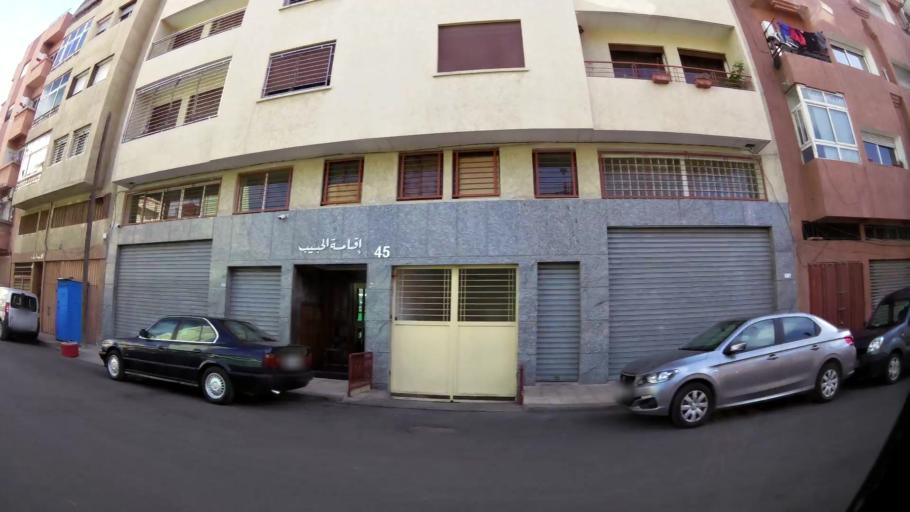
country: MA
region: Grand Casablanca
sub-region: Casablanca
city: Casablanca
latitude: 33.5899
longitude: -7.5795
